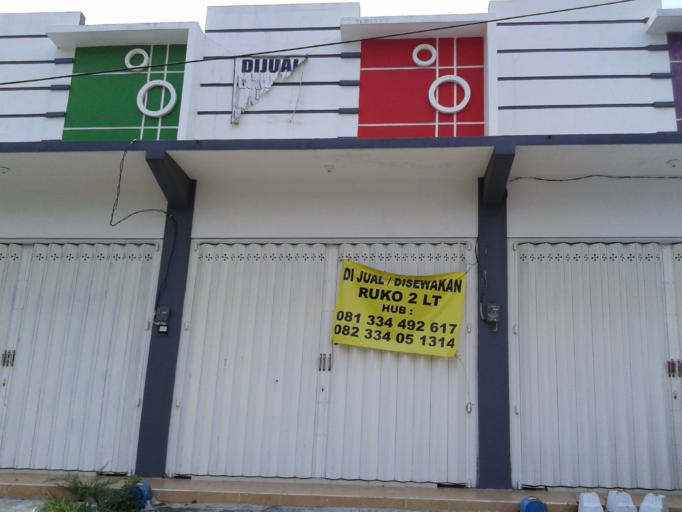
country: ID
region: East Java
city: Lawang
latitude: -7.8333
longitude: 112.6965
